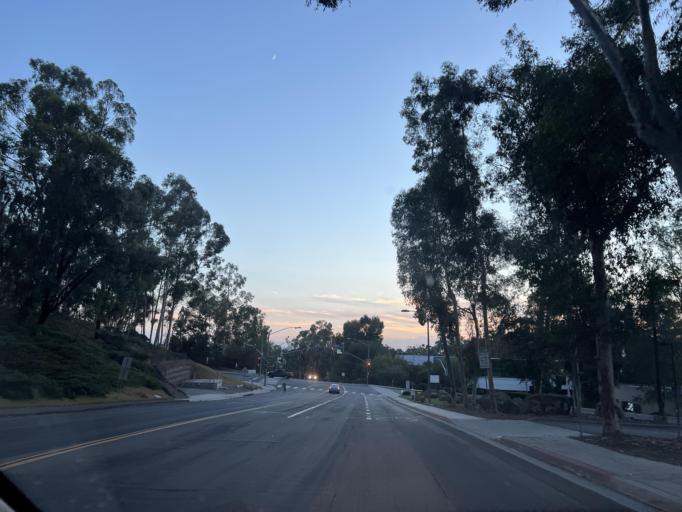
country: US
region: California
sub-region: San Diego County
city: Poway
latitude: 32.9118
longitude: -117.1087
